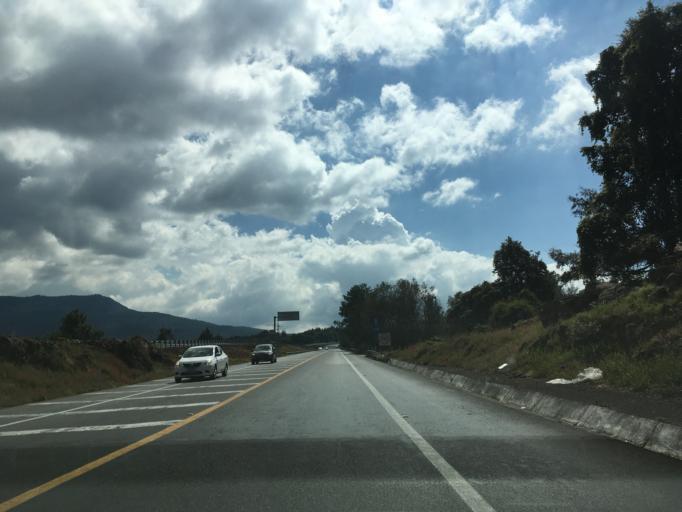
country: MX
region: Michoacan
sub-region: Patzcuaro
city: Colonia Vista Bella (Lomas del Peaje)
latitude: 19.5165
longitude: -101.5736
